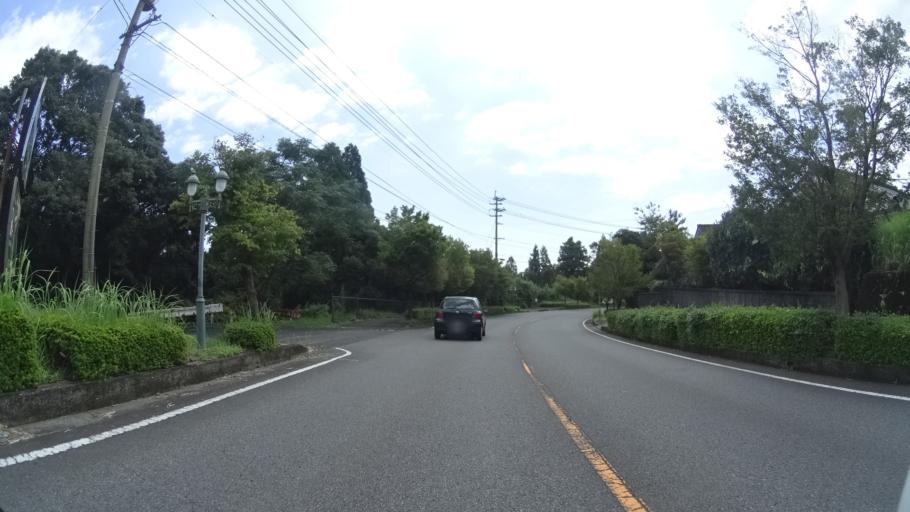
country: JP
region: Kagoshima
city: Kokubu-matsuki
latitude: 31.8873
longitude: 130.8212
